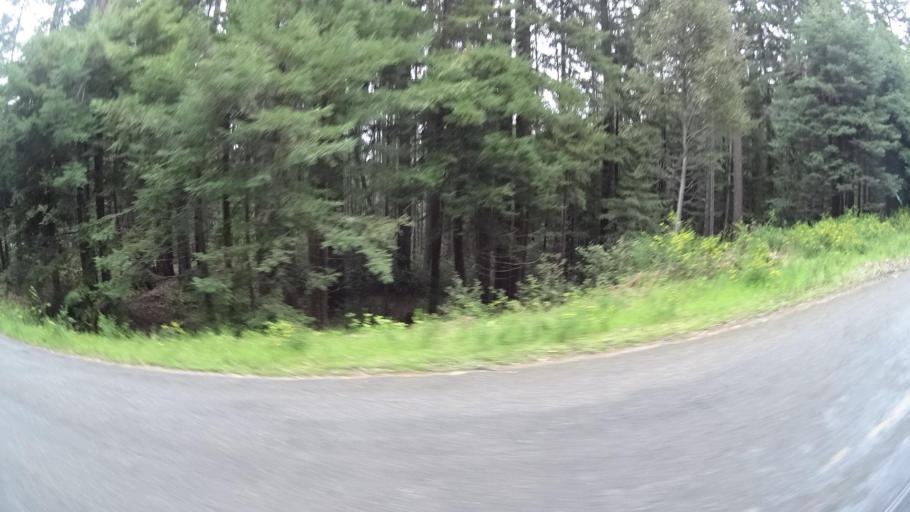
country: US
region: California
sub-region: Humboldt County
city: Redway
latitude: 40.2777
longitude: -123.7917
